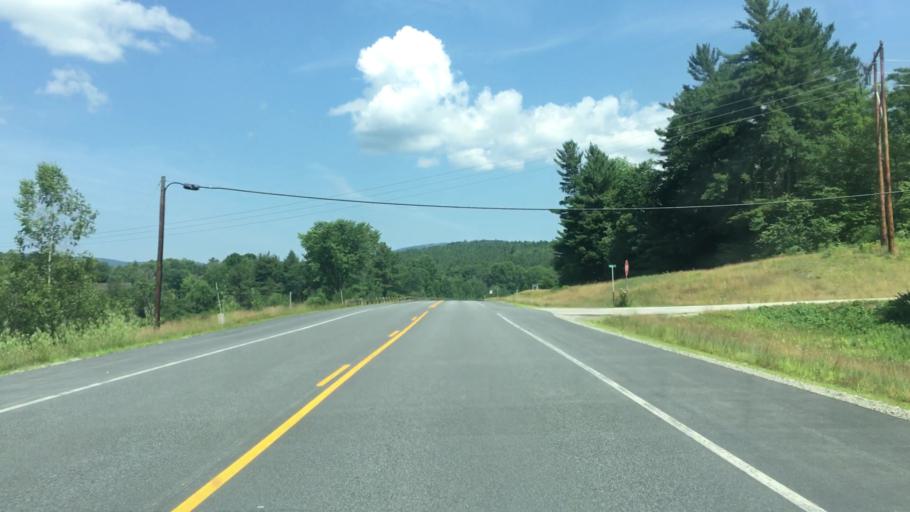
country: US
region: New Hampshire
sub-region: Sullivan County
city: Newport
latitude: 43.4095
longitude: -72.1869
